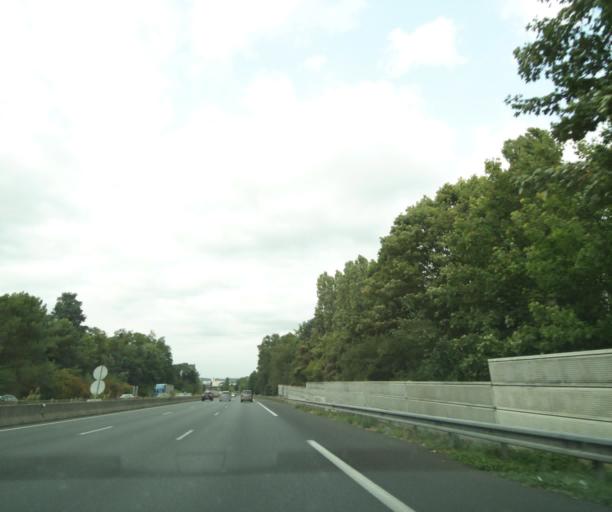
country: FR
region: Centre
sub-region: Departement d'Indre-et-Loire
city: Saint-Avertin
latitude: 47.3624
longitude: 0.7124
